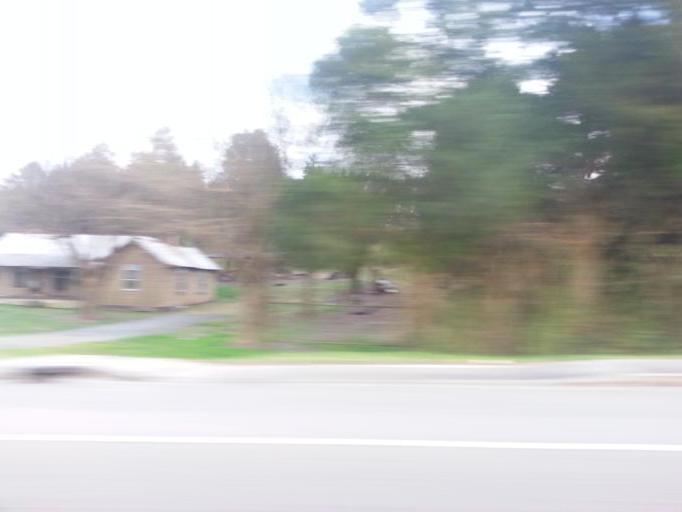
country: US
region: Tennessee
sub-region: Rhea County
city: Dayton
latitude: 35.5206
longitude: -84.9970
